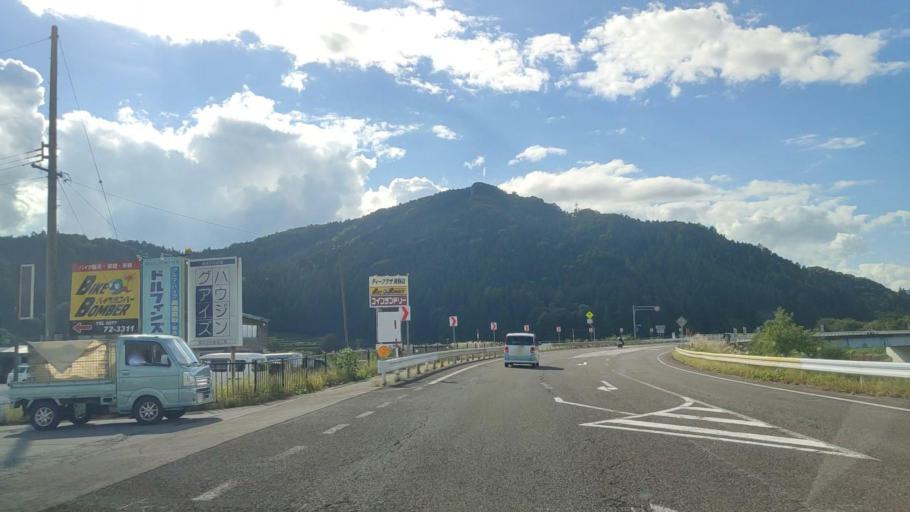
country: JP
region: Gifu
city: Takayama
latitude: 36.2089
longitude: 137.2130
